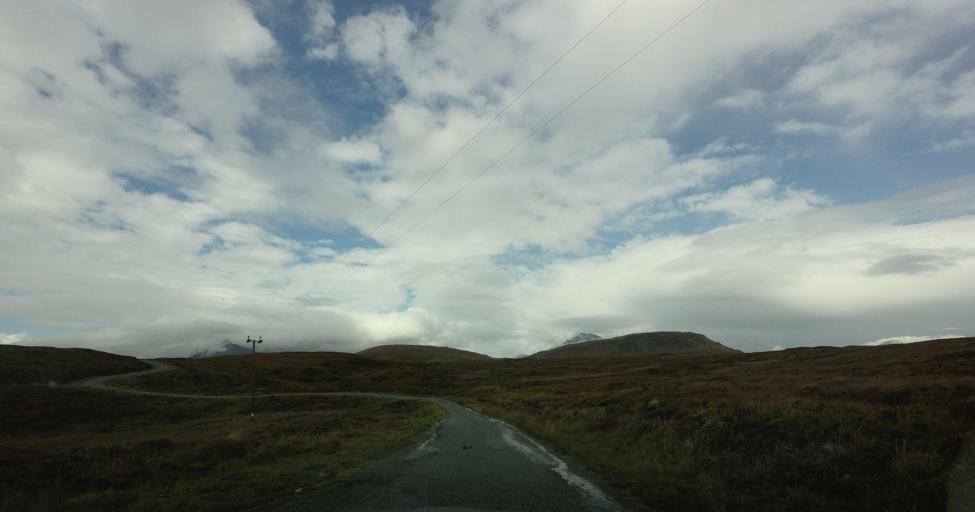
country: GB
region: Scotland
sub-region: Highland
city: Isle of Skye
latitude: 57.1429
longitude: -6.0763
